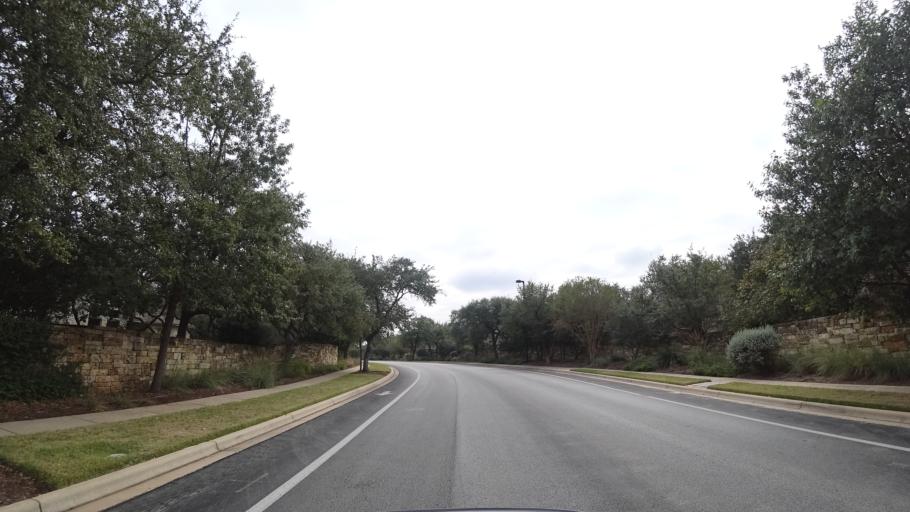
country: US
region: Texas
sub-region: Travis County
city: Shady Hollow
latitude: 30.1914
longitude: -97.9079
